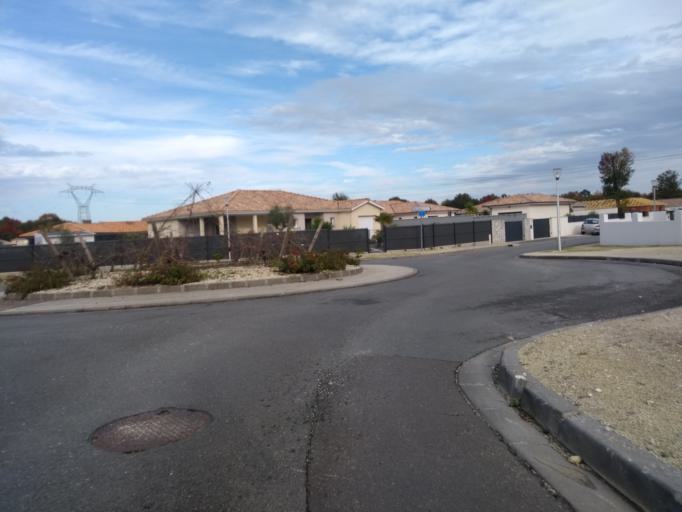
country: FR
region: Aquitaine
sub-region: Departement de la Gironde
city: Cestas
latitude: 44.7372
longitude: -0.6725
